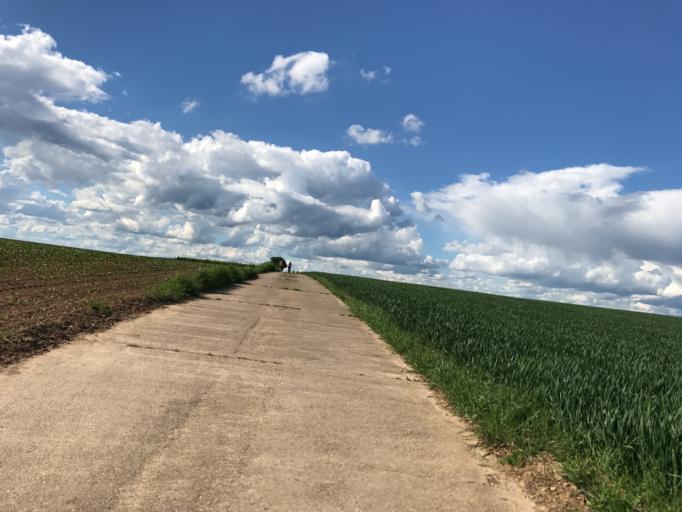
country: DE
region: Rheinland-Pfalz
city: Essenheim
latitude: 49.9457
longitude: 8.1294
